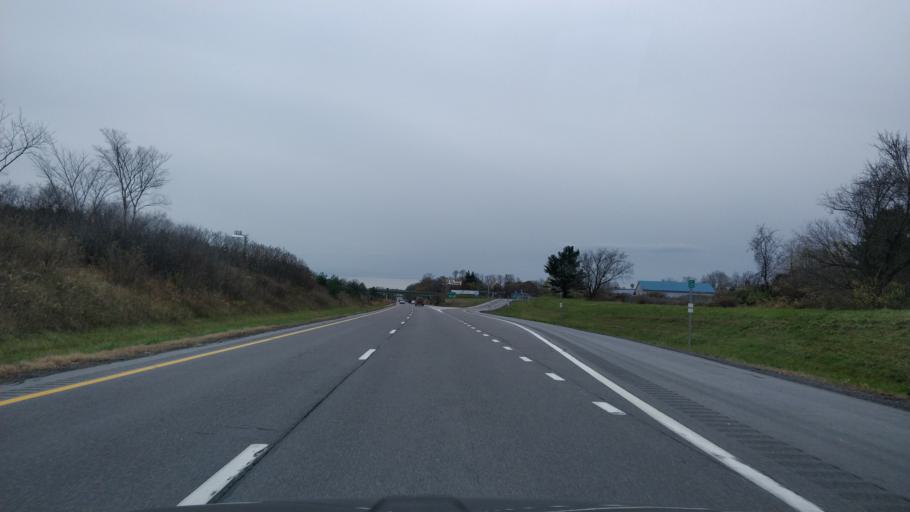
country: US
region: New York
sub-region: Oswego County
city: Pulaski
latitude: 43.5714
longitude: -76.1137
